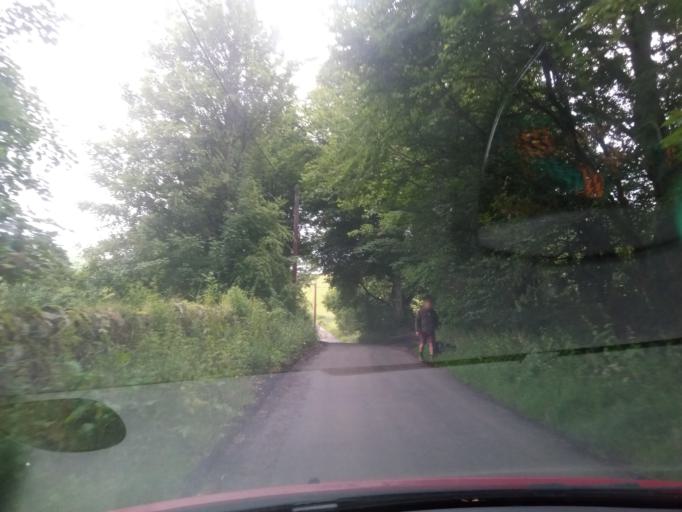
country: GB
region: Scotland
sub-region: Fife
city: Pathhead
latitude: 55.7655
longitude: -2.9438
